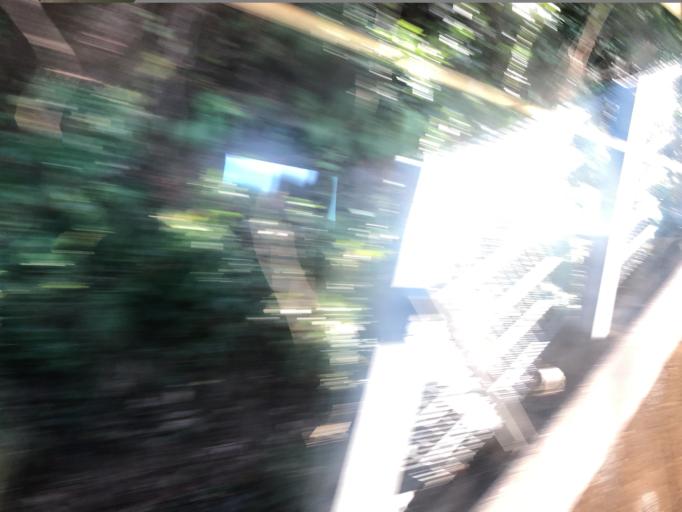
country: JP
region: Kochi
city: Nakamura
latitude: 33.0127
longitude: 132.9911
